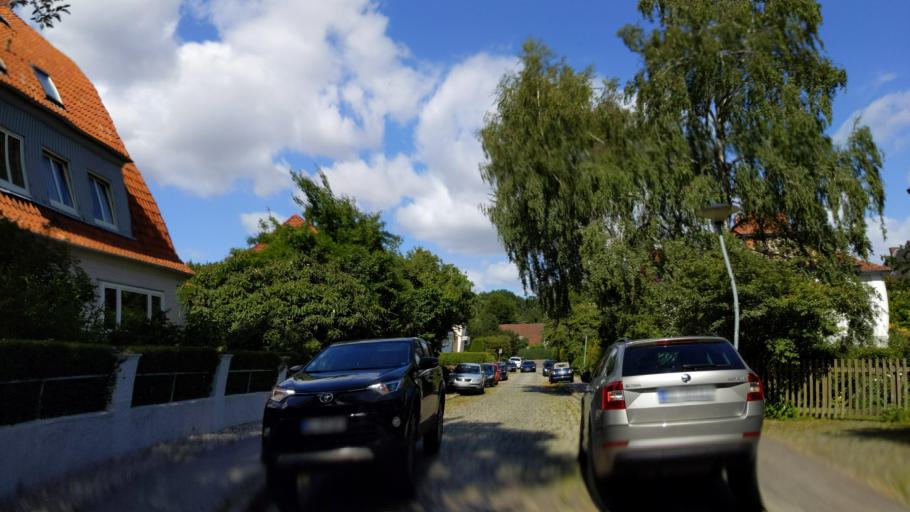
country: DE
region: Schleswig-Holstein
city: Luebeck
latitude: 53.8815
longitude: 10.7046
